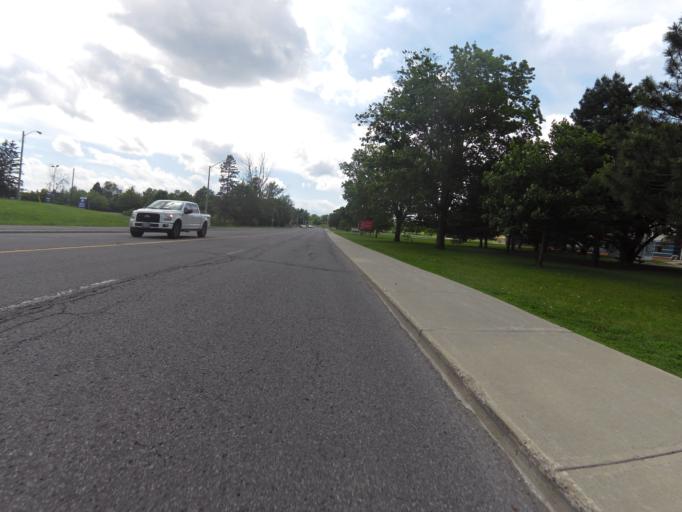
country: CA
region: Ontario
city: Ottawa
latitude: 45.3734
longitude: -75.6871
